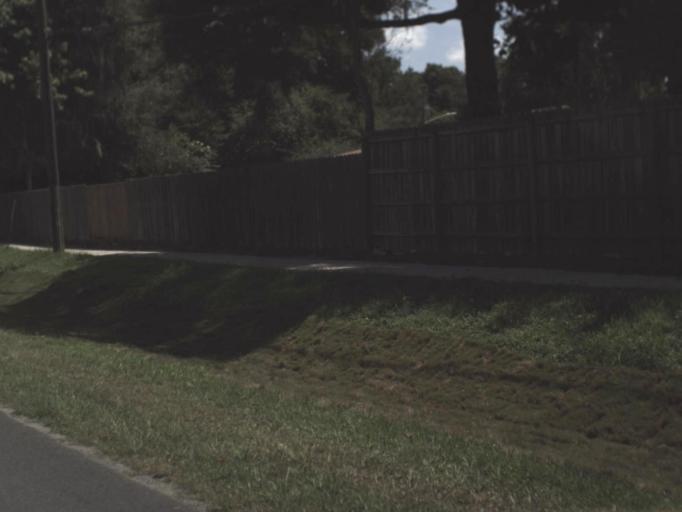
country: US
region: Florida
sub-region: Alachua County
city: Gainesville
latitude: 29.6970
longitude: -82.3722
